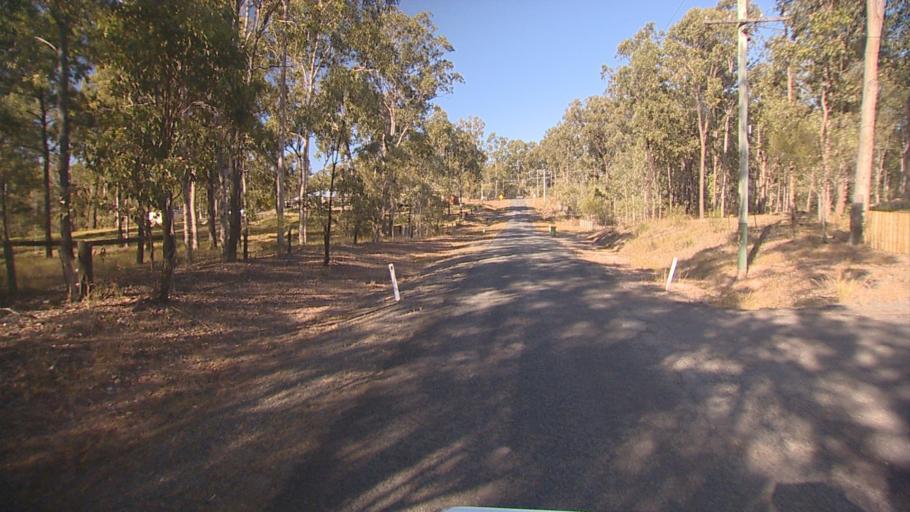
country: AU
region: Queensland
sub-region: Ipswich
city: Springfield Lakes
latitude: -27.6912
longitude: 152.9296
